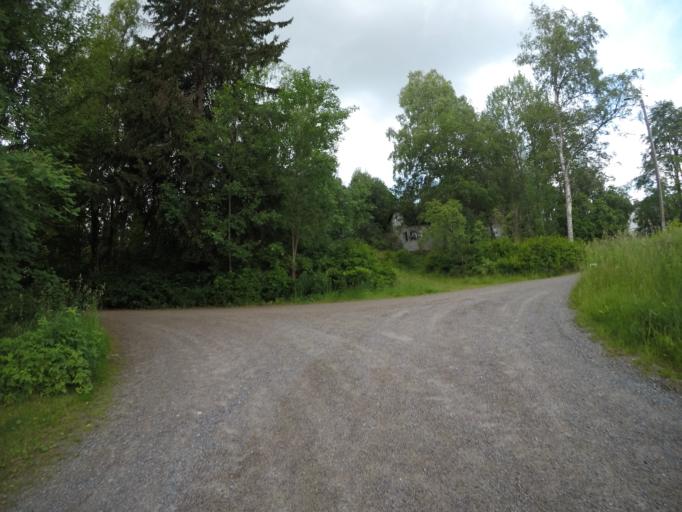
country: FI
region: Haeme
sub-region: Haemeenlinna
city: Haemeenlinna
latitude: 60.9744
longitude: 24.4353
